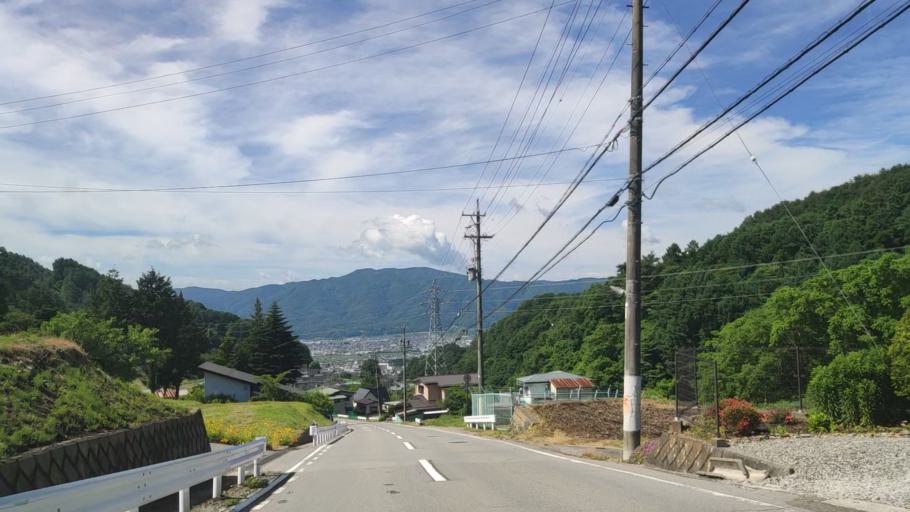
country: JP
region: Nagano
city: Suwa
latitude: 36.0578
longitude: 138.1301
